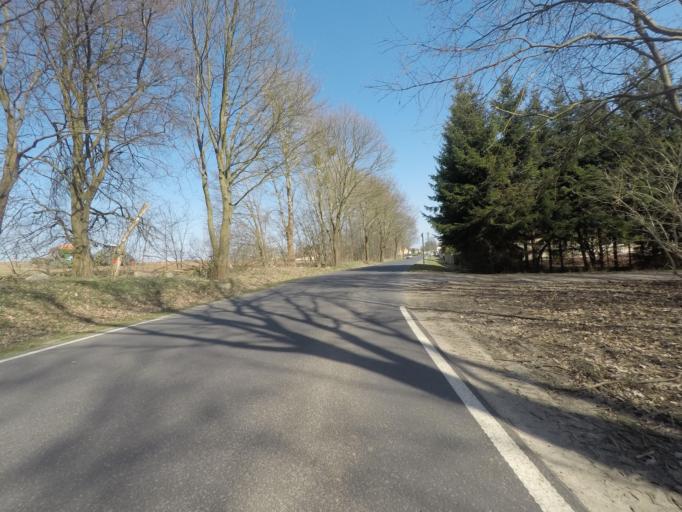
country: DE
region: Brandenburg
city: Britz
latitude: 52.8678
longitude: 13.7290
